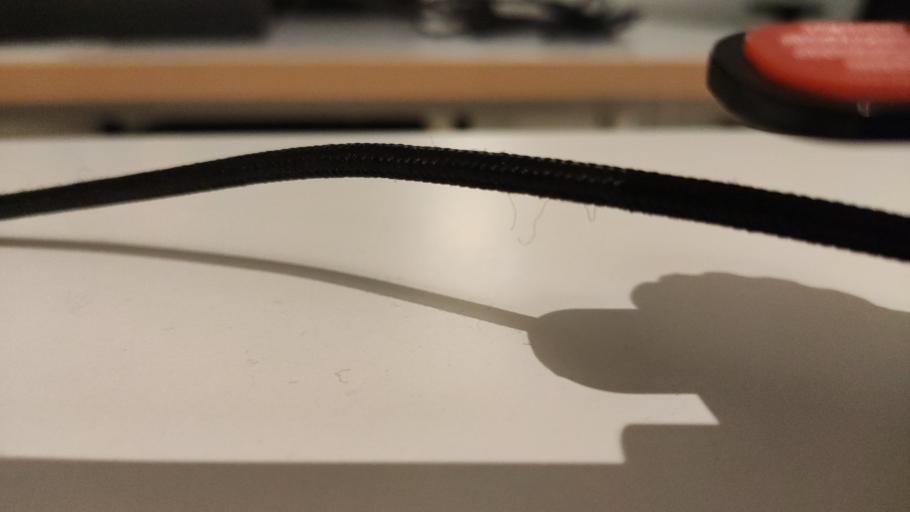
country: RU
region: Moskovskaya
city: Novosin'kovo
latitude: 56.3709
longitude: 37.3525
